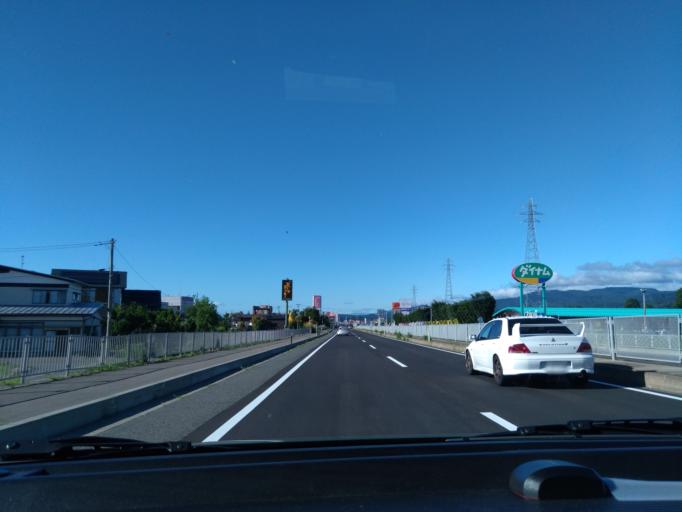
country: JP
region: Akita
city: Yokotemachi
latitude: 39.2921
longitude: 140.5531
